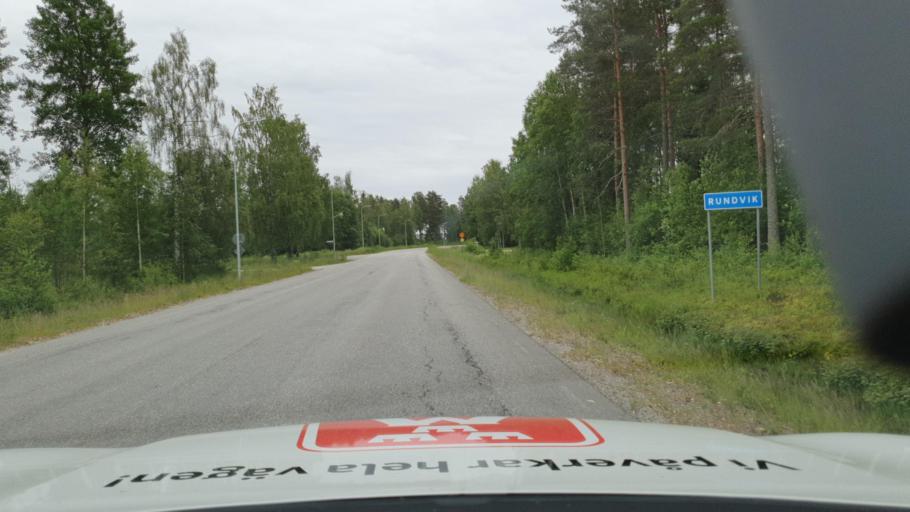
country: SE
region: Vaesterbotten
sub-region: Nordmalings Kommun
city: Nordmaling
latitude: 63.5472
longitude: 19.4311
